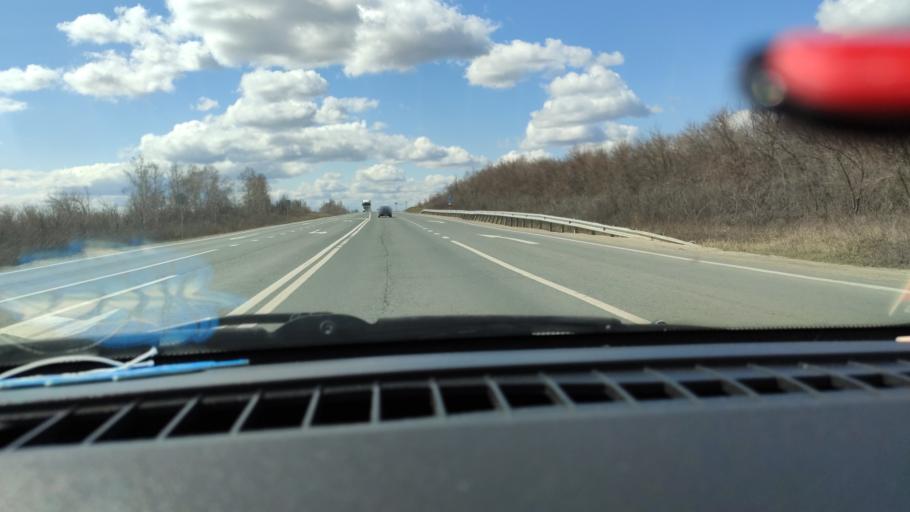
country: RU
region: Saratov
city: Dukhovnitskoye
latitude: 52.6769
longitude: 48.2284
